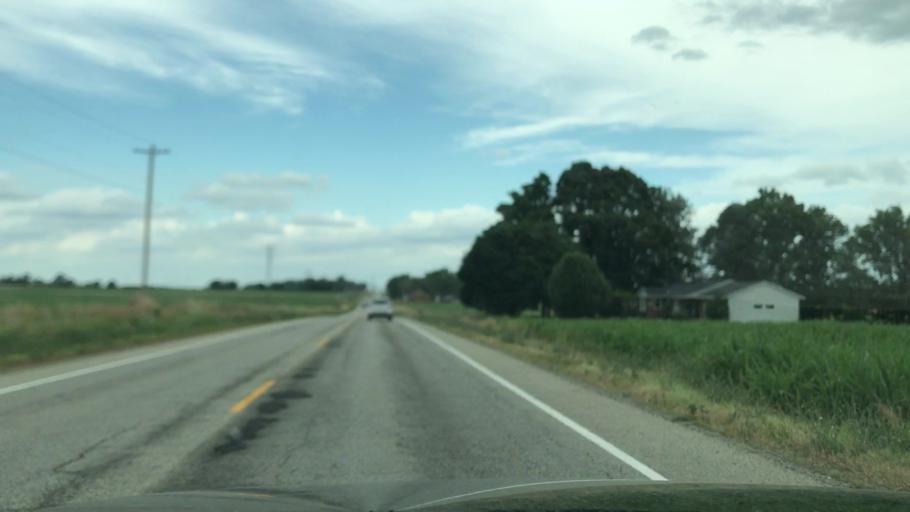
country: US
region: Michigan
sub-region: Ottawa County
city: Hudsonville
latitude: 42.8211
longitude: -85.8619
